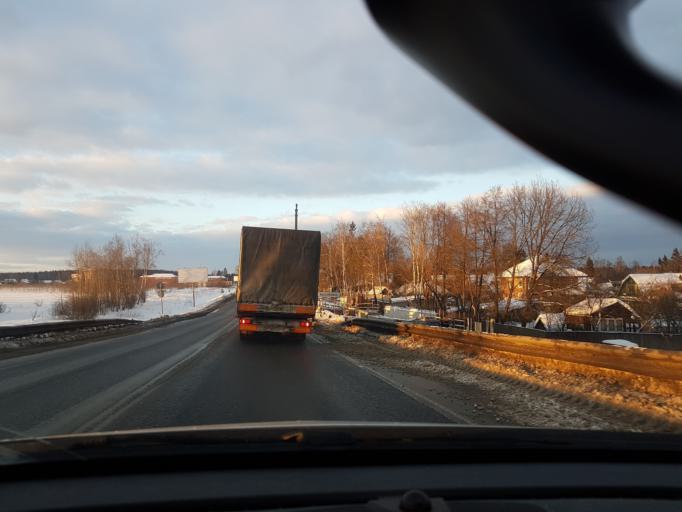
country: RU
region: Moskovskaya
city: Istra
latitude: 55.9000
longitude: 36.9449
